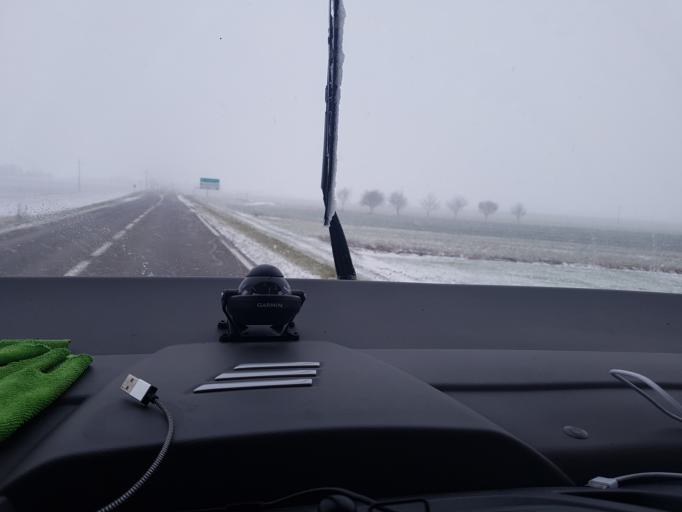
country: FR
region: Lorraine
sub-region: Departement de la Moselle
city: Chateau-Salins
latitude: 48.8702
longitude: 6.4227
